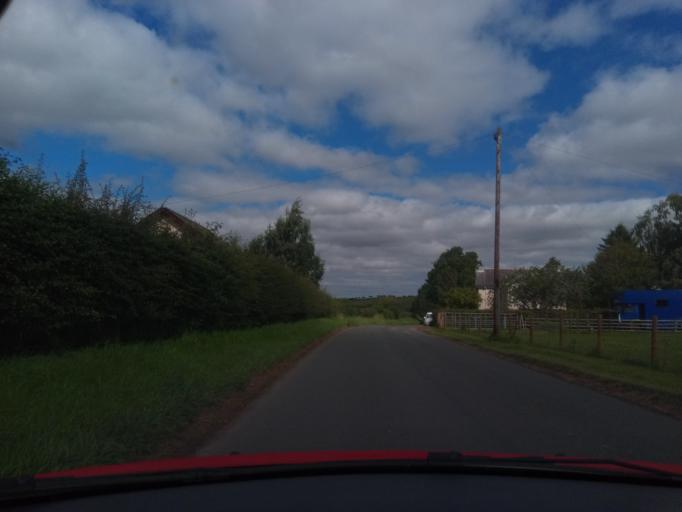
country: GB
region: Scotland
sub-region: The Scottish Borders
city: Kelso
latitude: 55.5351
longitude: -2.3628
